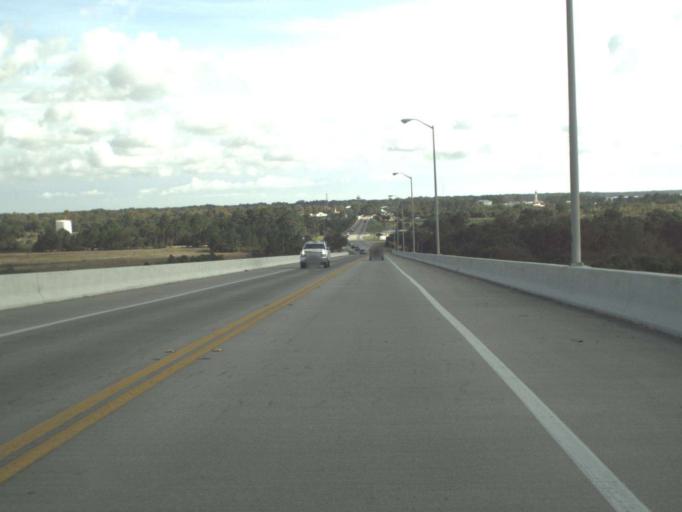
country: US
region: Florida
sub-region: Gulf County
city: Port Saint Joe
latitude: 29.8312
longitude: -85.3129
